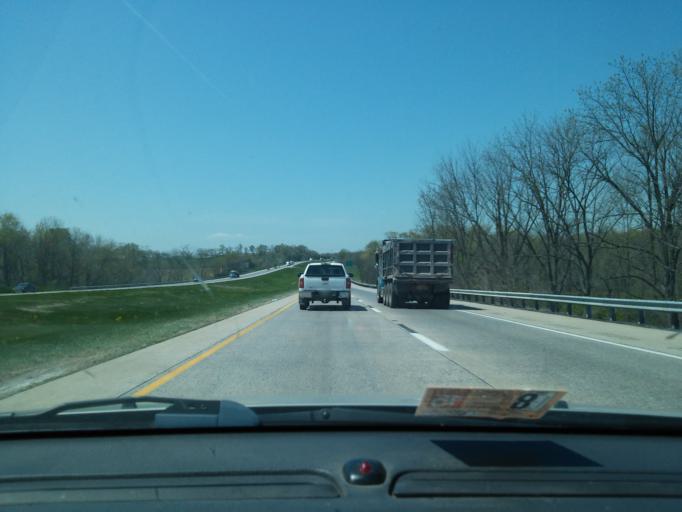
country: US
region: Pennsylvania
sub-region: Lebanon County
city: Jonestown
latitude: 40.4184
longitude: -76.5515
